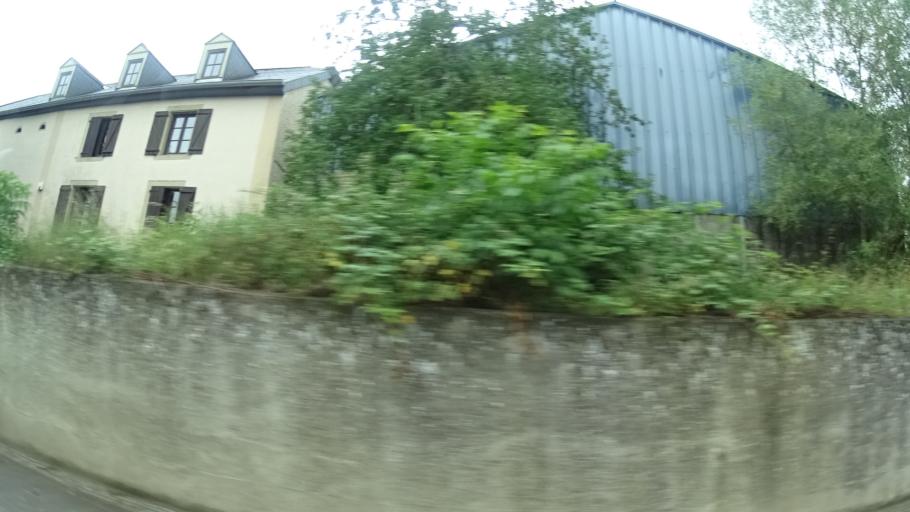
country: LU
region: Luxembourg
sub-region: Canton d'Esch-sur-Alzette
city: Mondercange
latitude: 49.5314
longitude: 5.9852
